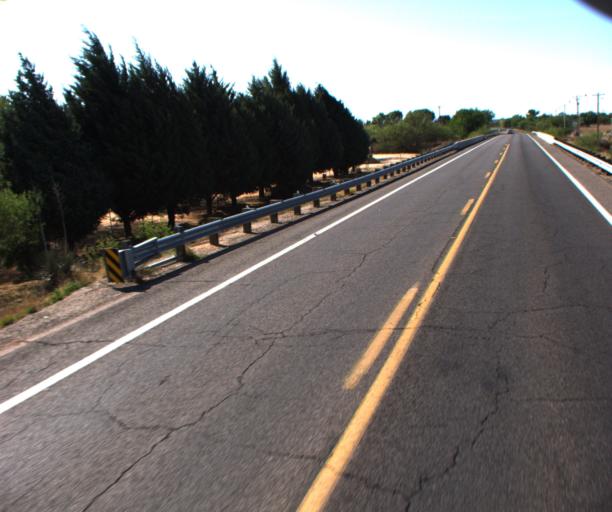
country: US
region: Arizona
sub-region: Cochise County
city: Saint David
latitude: 31.8706
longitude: -110.2086
